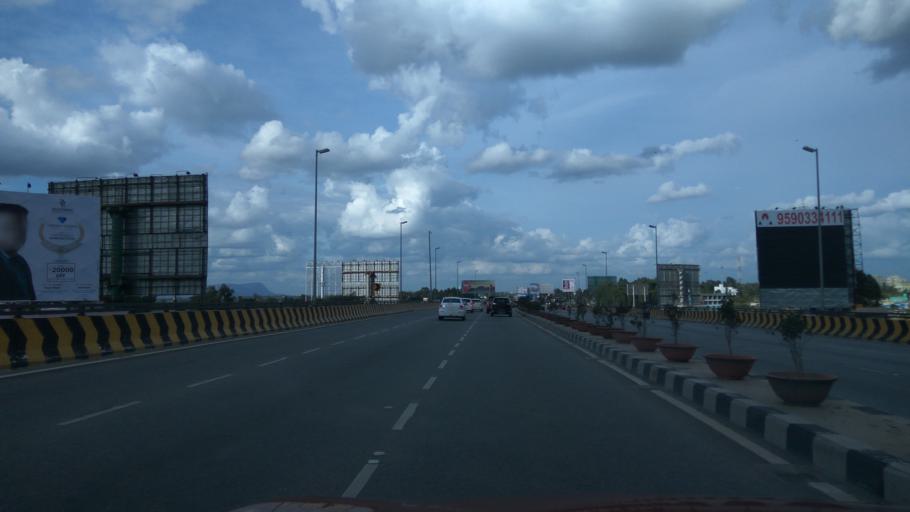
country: IN
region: Karnataka
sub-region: Bangalore Urban
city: Yelahanka
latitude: 13.1604
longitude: 77.6261
